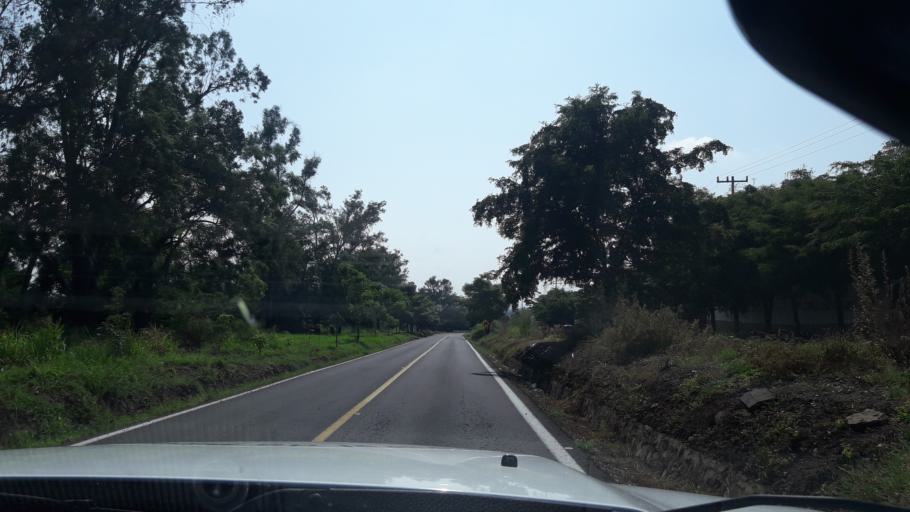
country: MX
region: Colima
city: Comala
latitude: 19.3335
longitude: -103.7478
